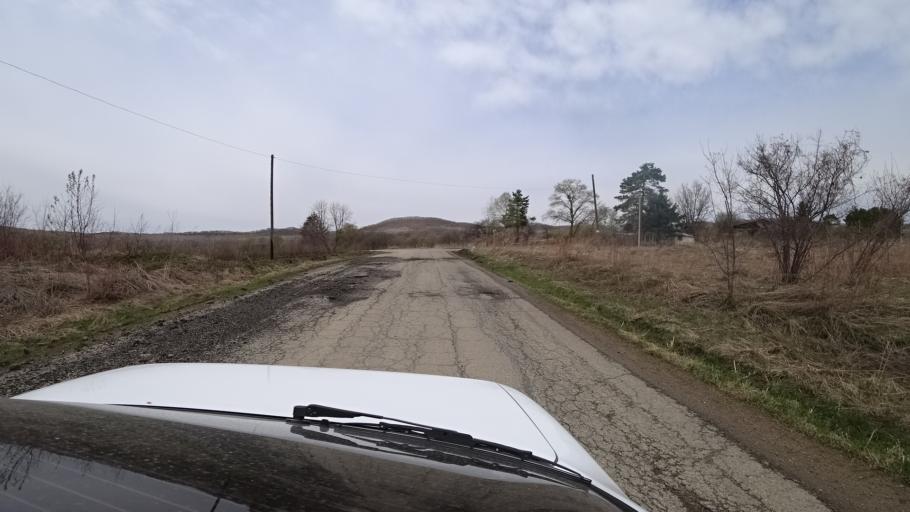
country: RU
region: Primorskiy
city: Dal'nerechensk
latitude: 45.7991
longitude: 134.1009
